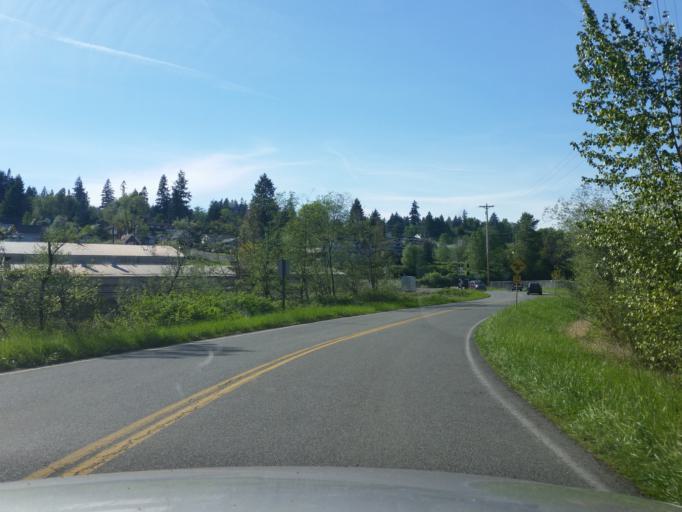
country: US
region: Washington
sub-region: Snohomish County
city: Everett
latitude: 47.9464
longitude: -122.1903
